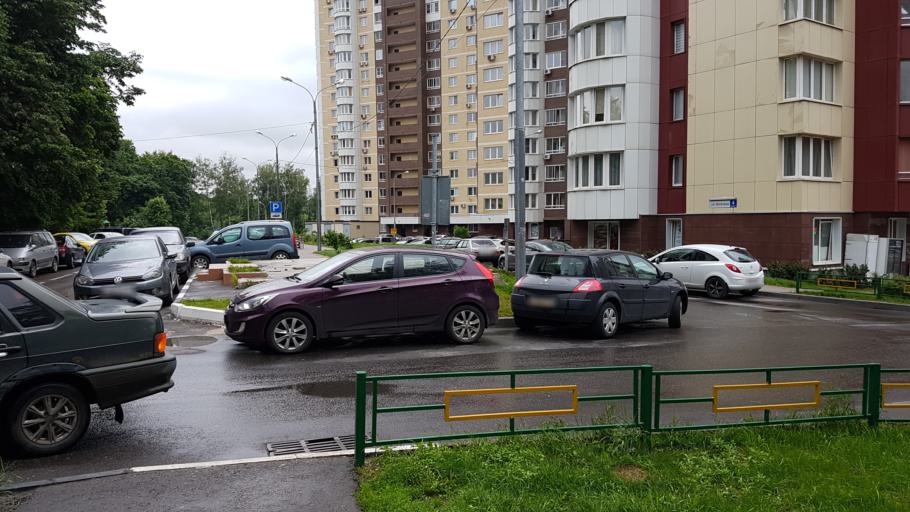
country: RU
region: Moscow
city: Khimki
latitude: 55.8874
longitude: 37.4555
